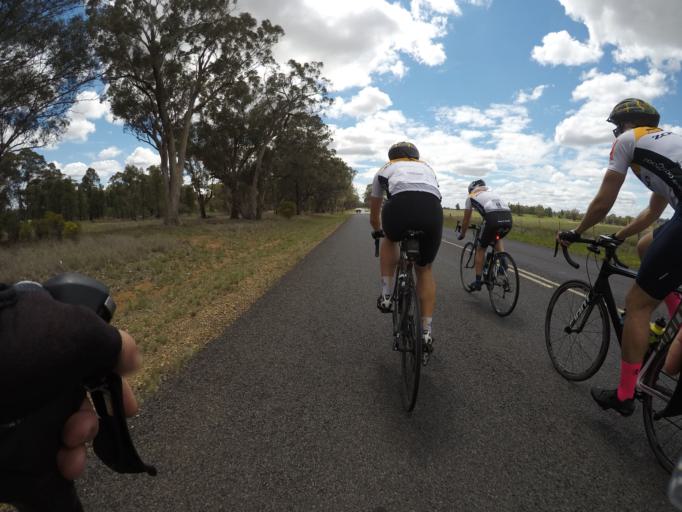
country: AU
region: New South Wales
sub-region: Dubbo Municipality
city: Dubbo
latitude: -32.4619
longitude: 148.5730
